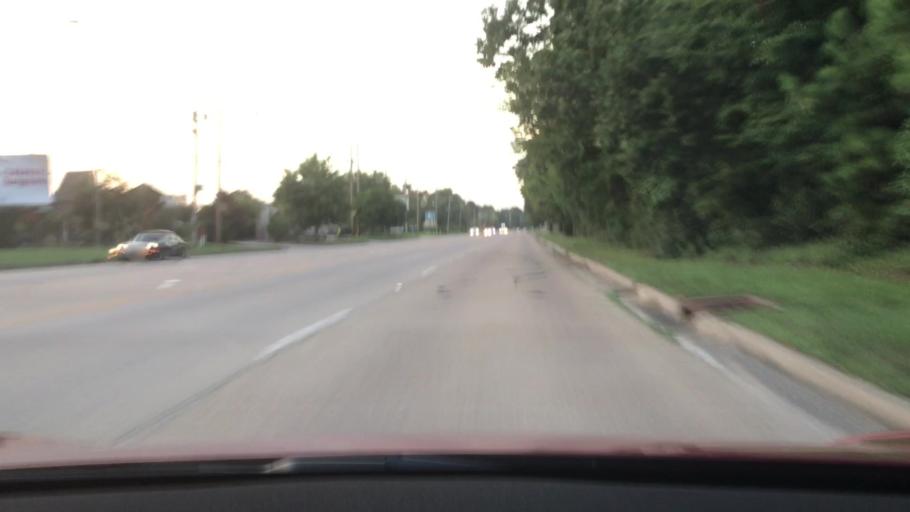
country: US
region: Louisiana
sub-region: Bossier Parish
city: Bossier City
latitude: 32.4072
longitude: -93.7385
